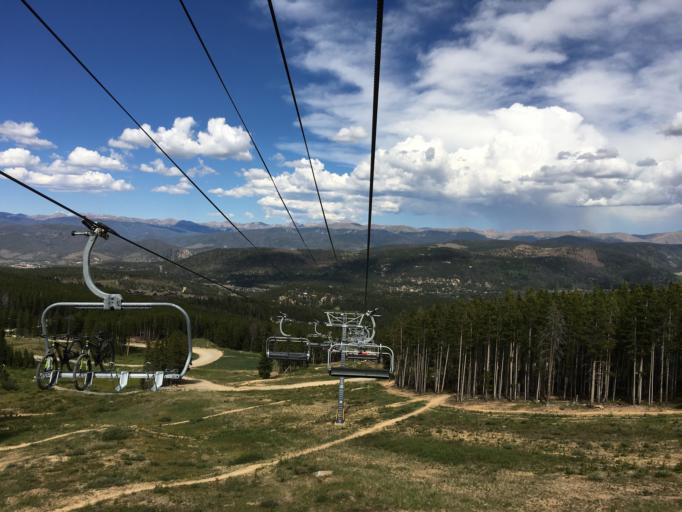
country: US
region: Colorado
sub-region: Summit County
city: Breckenridge
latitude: 39.4757
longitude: -106.0767
